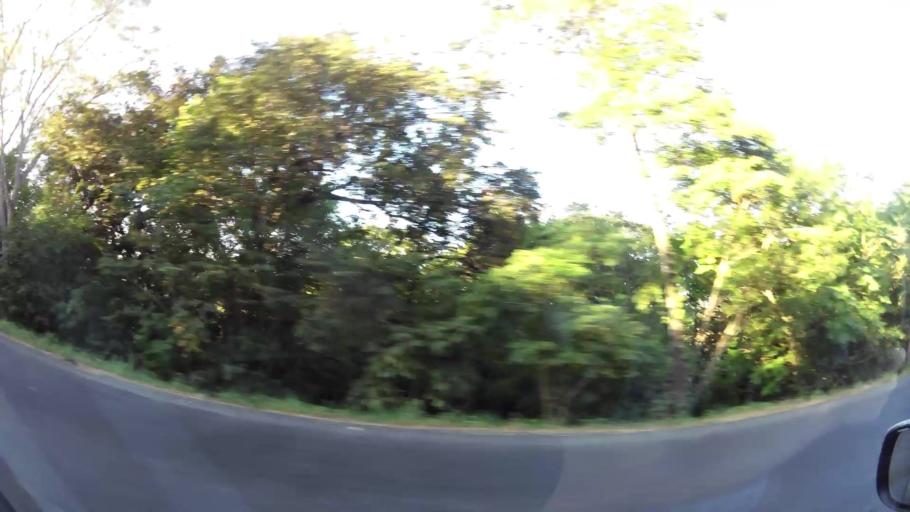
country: CR
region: Puntarenas
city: Esparza
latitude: 10.0045
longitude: -84.7213
